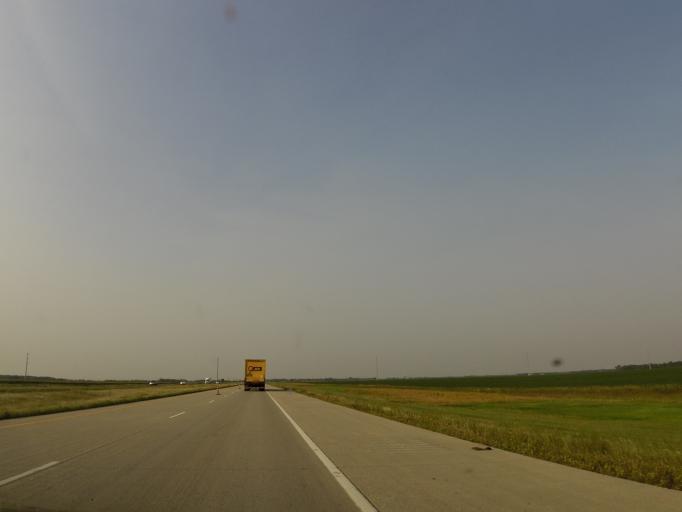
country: US
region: North Dakota
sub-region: Cass County
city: Horace
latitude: 46.6758
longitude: -96.8308
